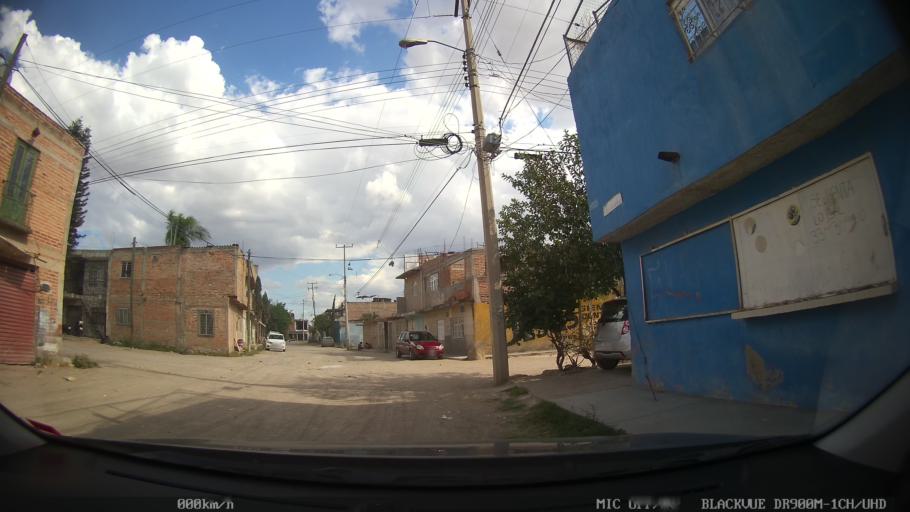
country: MX
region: Jalisco
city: Tlaquepaque
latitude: 20.6615
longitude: -103.2662
